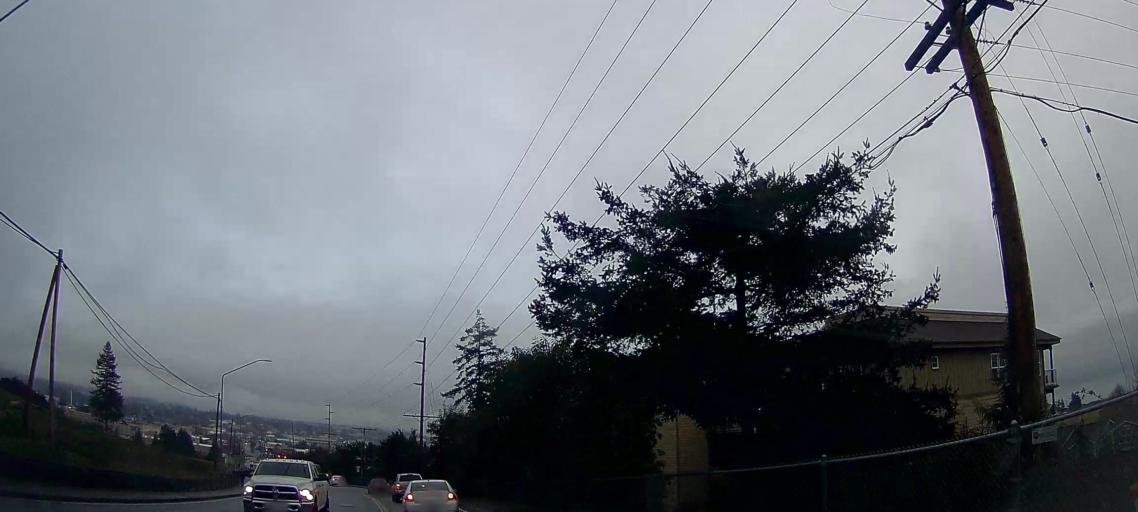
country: US
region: Washington
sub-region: Island County
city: Oak Harbor
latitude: 48.2840
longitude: -122.6659
